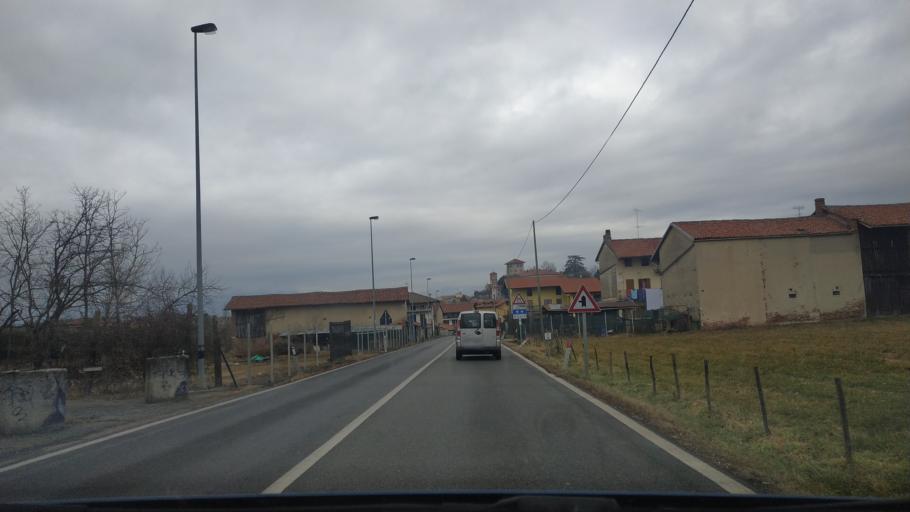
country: IT
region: Piedmont
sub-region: Provincia di Torino
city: Mercenasco
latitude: 45.3520
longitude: 7.8829
